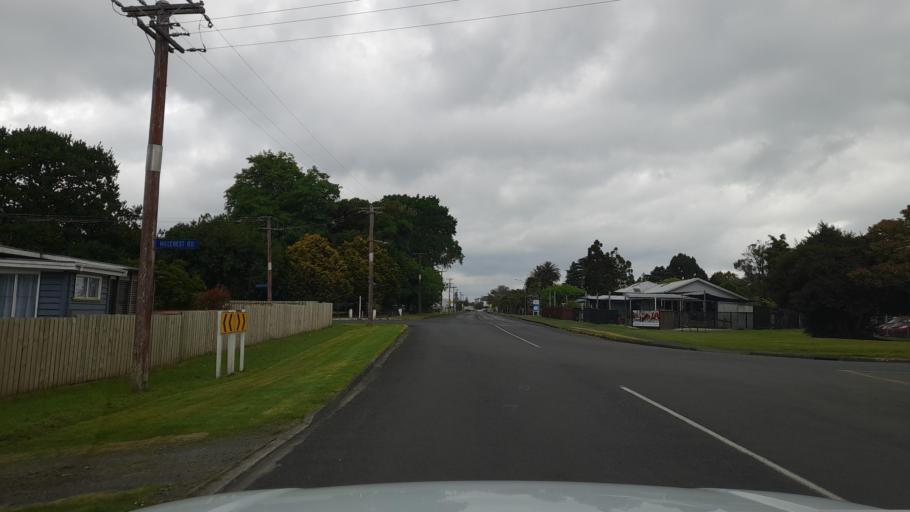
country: NZ
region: Northland
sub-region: Far North District
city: Waimate North
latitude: -35.4048
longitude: 173.7962
